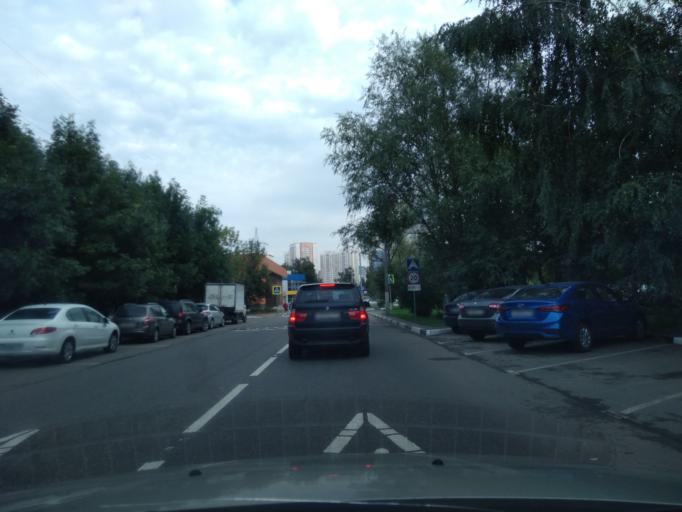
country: RU
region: Moscow
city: Khimki
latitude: 55.8815
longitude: 37.4248
